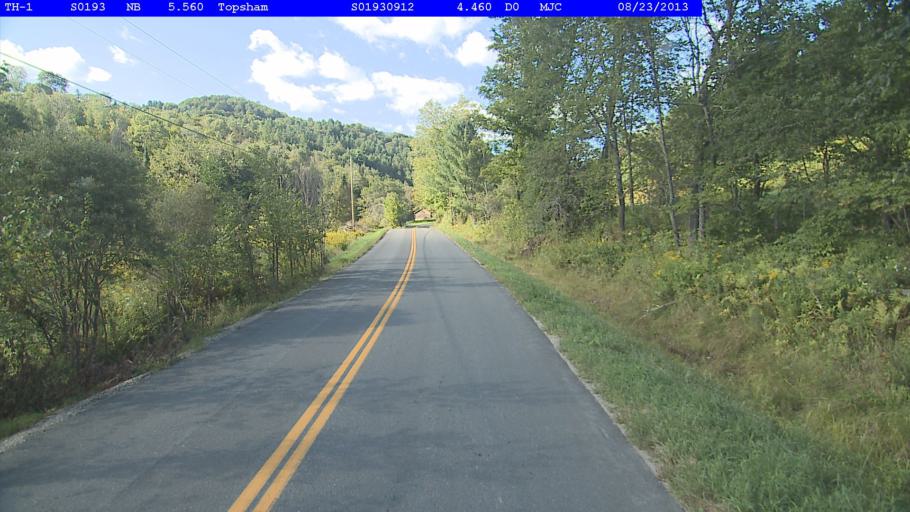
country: US
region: New Hampshire
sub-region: Grafton County
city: Haverhill
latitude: 44.1277
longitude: -72.2430
